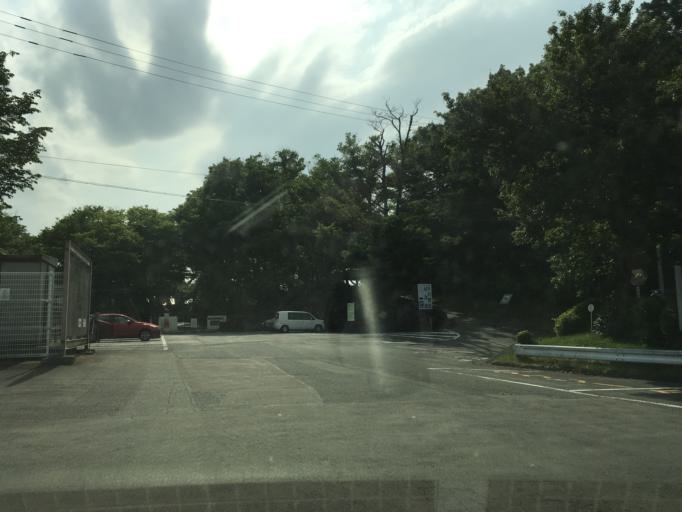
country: JP
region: Iwate
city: Hanamaki
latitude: 39.3996
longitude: 141.1641
